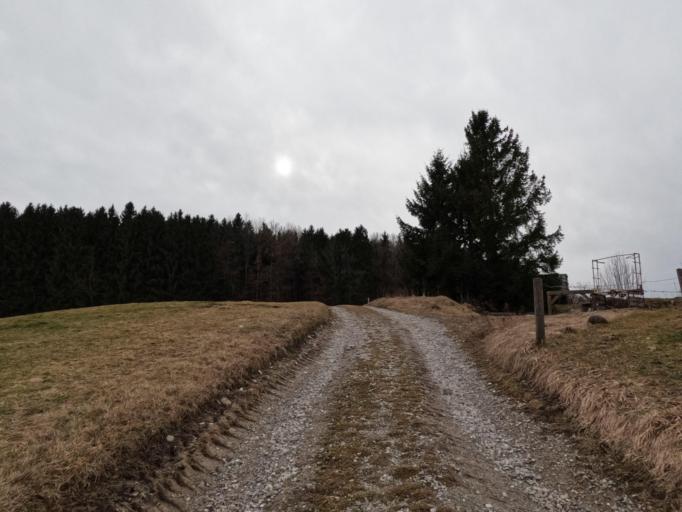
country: DE
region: Bavaria
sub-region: Upper Bavaria
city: Vachendorf
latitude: 47.8493
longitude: 12.5924
